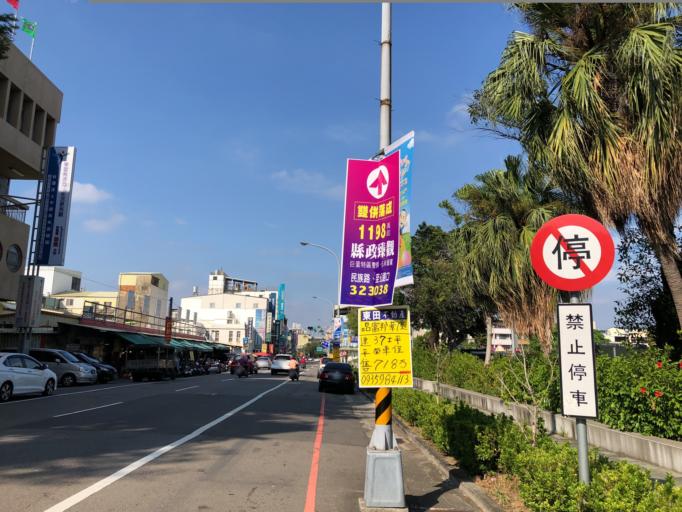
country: TW
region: Taiwan
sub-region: Miaoli
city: Miaoli
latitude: 24.5613
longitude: 120.8227
